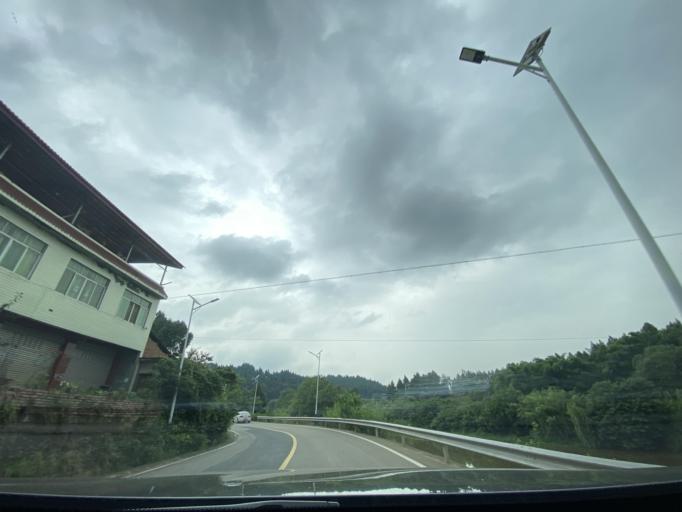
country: CN
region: Sichuan
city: Jiancheng
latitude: 30.5531
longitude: 104.5225
